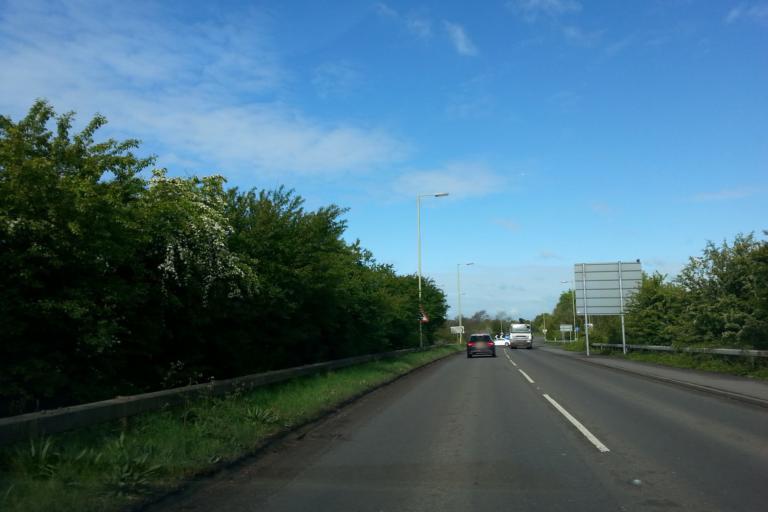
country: GB
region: England
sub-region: Staffordshire
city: Alrewas
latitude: 52.7266
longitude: -1.7472
